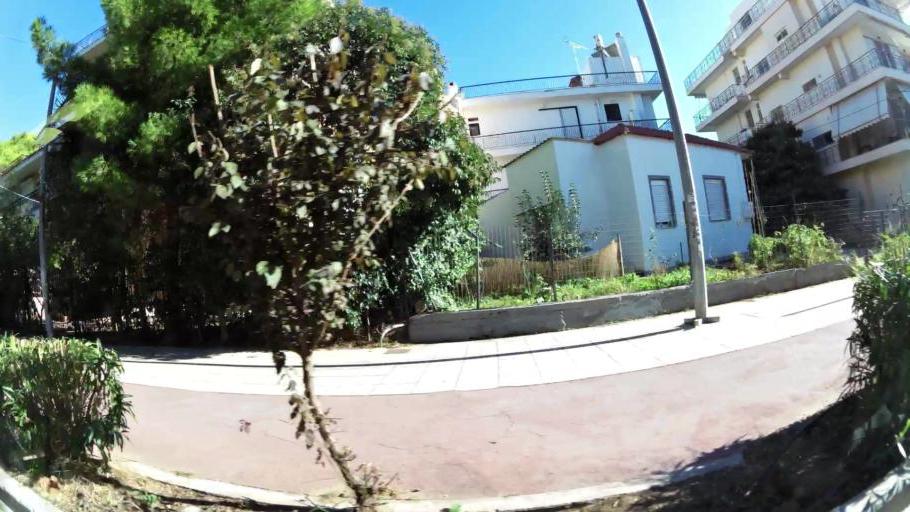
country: GR
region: Attica
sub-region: Nomarchia Athinas
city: Vrilissia
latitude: 38.0400
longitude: 23.8323
